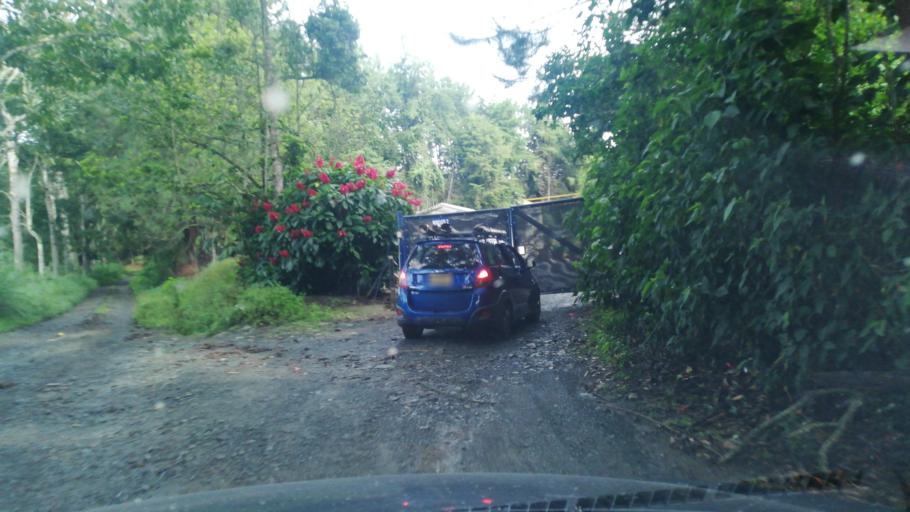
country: CO
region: Valle del Cauca
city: Restrepo
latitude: 3.8530
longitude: -76.4651
